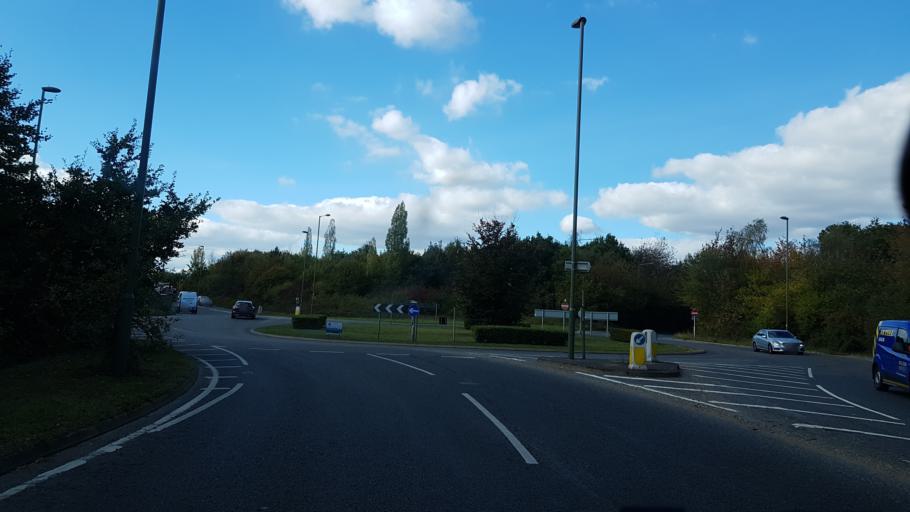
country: GB
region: England
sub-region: Surrey
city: Milford
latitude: 51.1781
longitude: -0.6500
